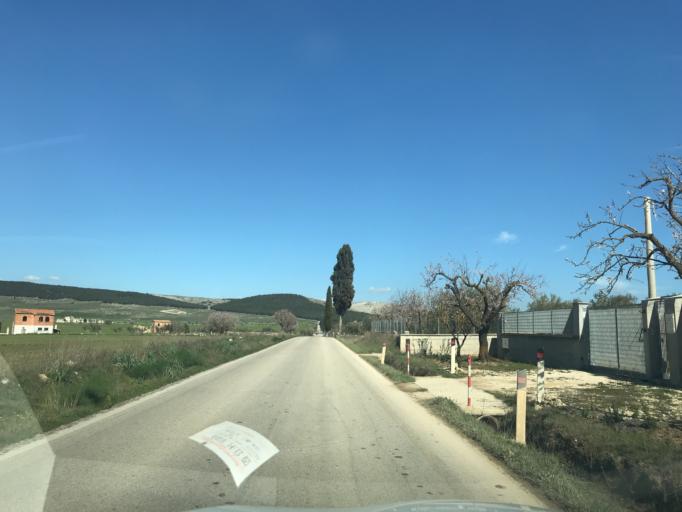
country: IT
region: Apulia
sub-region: Provincia di Bari
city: Gravina in Puglia
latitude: 40.8558
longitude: 16.4329
